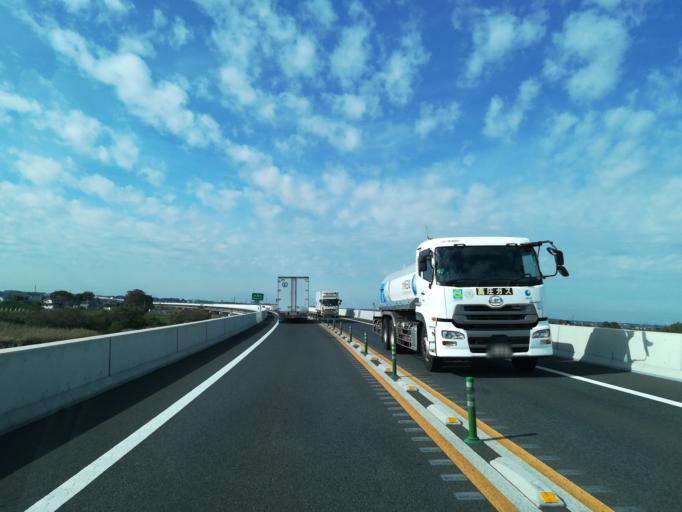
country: JP
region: Ibaraki
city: Ishige
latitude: 36.0800
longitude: 140.0060
